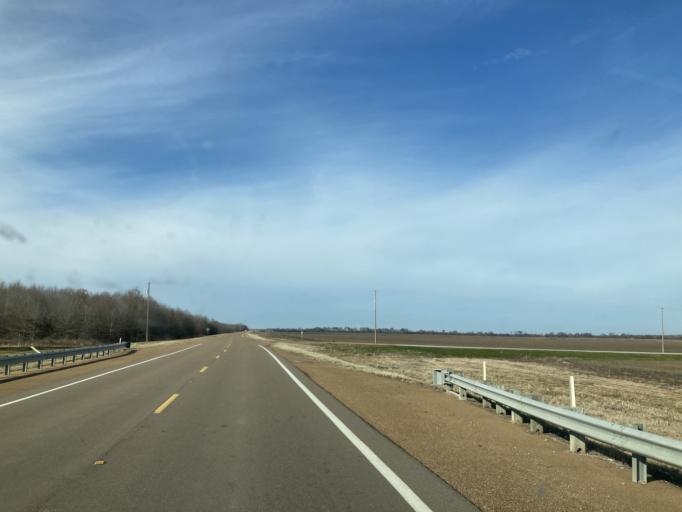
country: US
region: Mississippi
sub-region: Humphreys County
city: Belzoni
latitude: 32.9956
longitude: -90.6212
